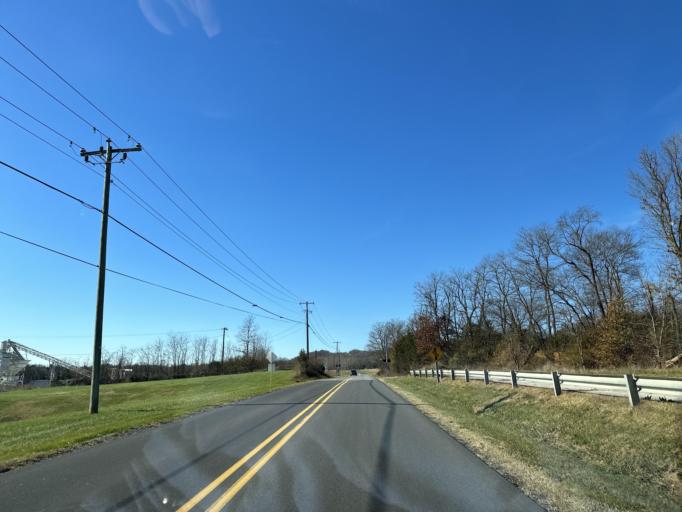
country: US
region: Virginia
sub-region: Augusta County
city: Weyers Cave
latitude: 38.2670
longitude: -78.9464
